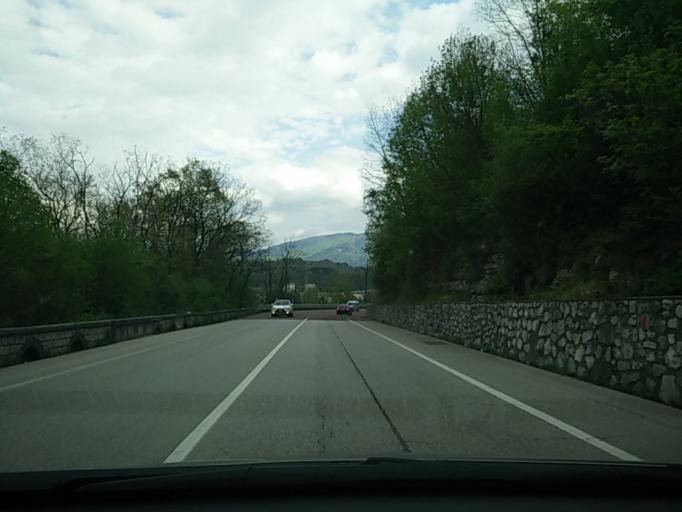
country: IT
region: Veneto
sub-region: Provincia di Belluno
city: Soccher-Paiane-Casan-Arsie
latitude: 46.1622
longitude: 12.3189
